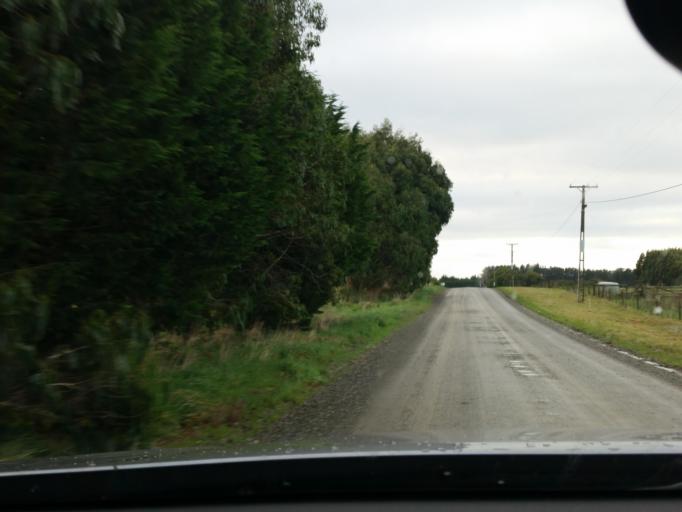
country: NZ
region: Southland
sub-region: Invercargill City
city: Invercargill
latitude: -46.3557
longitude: 168.4474
